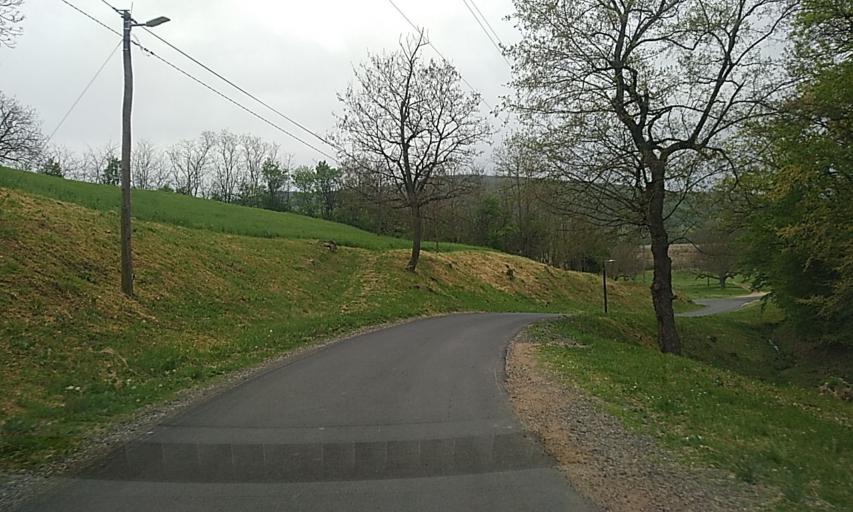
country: RS
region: Central Serbia
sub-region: Nisavski Okrug
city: Razanj
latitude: 43.6214
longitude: 21.5270
